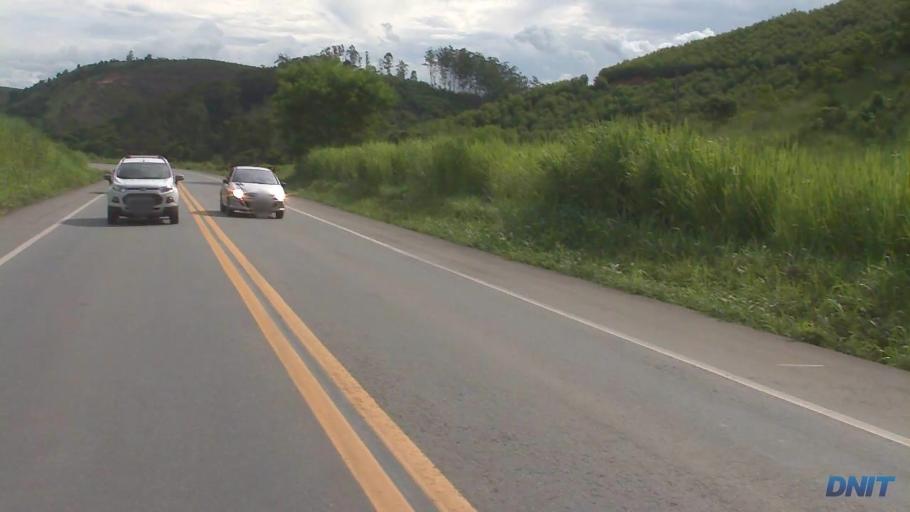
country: BR
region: Minas Gerais
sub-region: Belo Oriente
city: Belo Oriente
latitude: -19.2718
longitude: -42.3566
